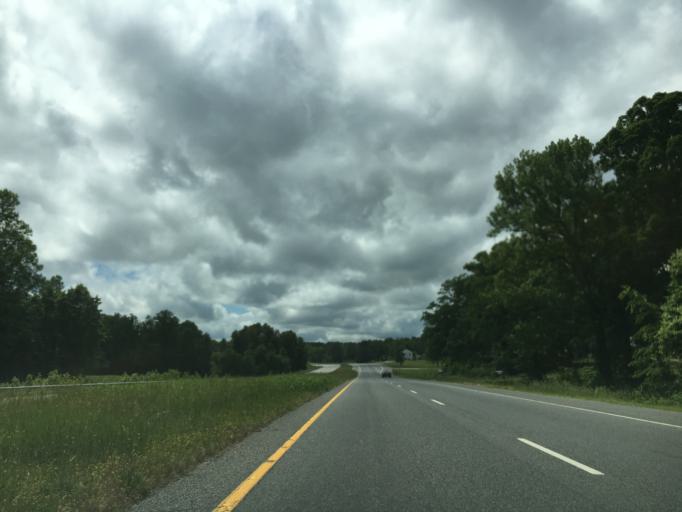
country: US
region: Virginia
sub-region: Mecklenburg County
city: Clarksville
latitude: 36.6511
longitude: -78.4878
